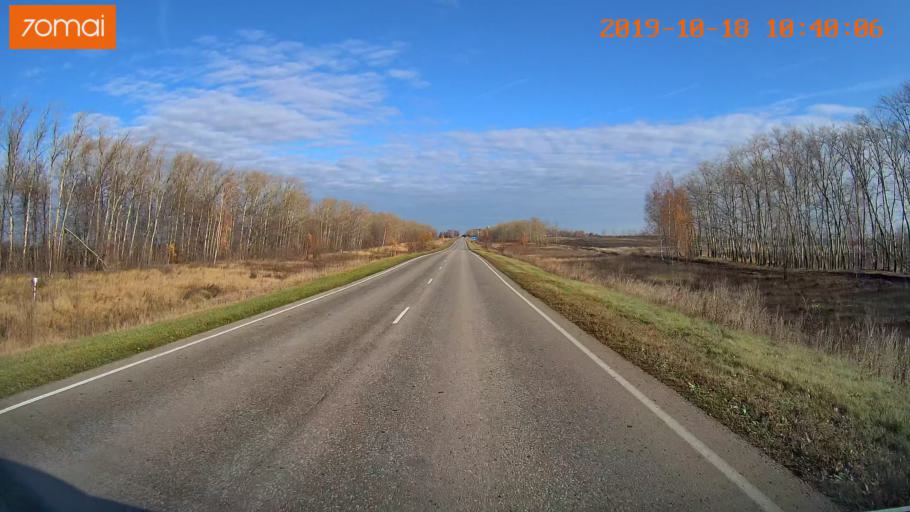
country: RU
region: Tula
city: Kurkino
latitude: 53.5965
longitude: 38.6610
